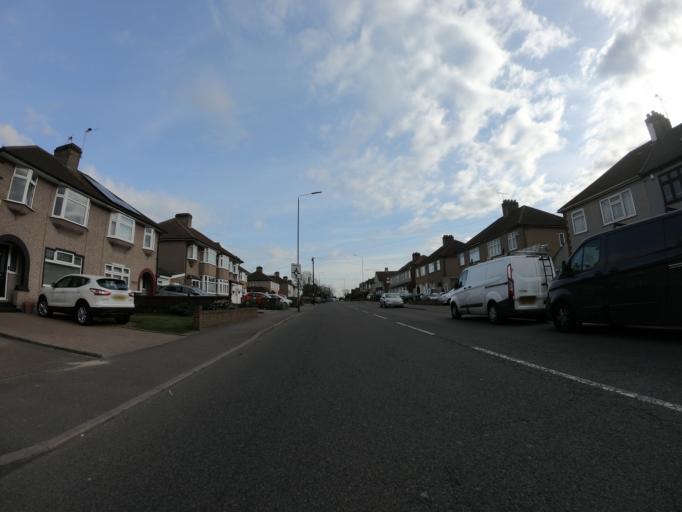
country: GB
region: England
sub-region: Greater London
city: Bexleyheath
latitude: 51.4749
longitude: 0.1448
